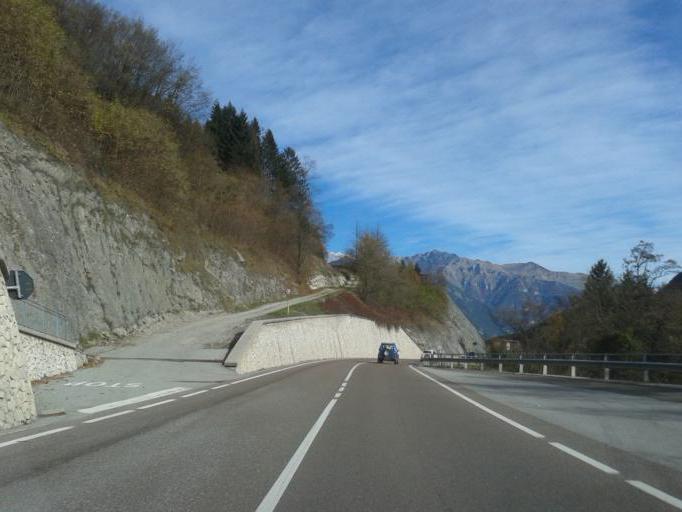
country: IT
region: Trentino-Alto Adige
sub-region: Provincia di Trento
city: Breguzzo
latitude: 46.0131
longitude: 10.7038
